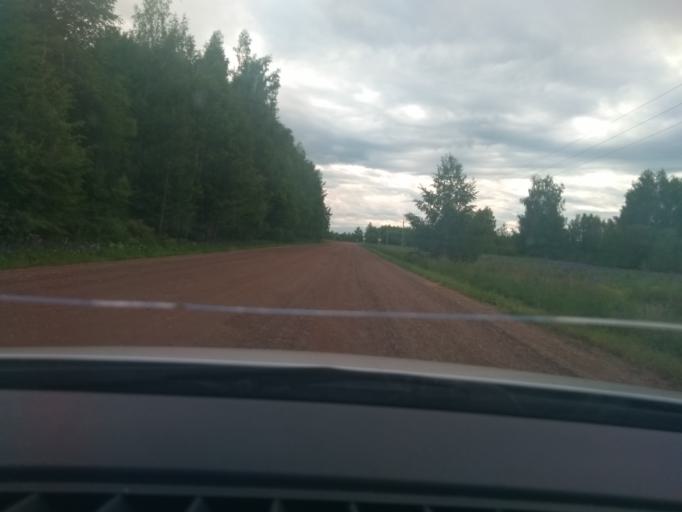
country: RU
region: Perm
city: Sylva
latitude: 57.8175
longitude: 56.7244
